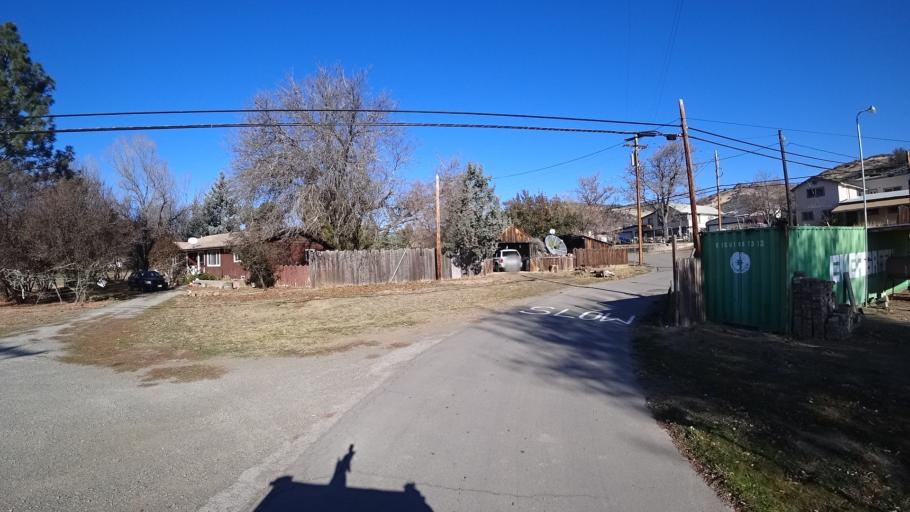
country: US
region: California
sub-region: Siskiyou County
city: Montague
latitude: 41.9112
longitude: -122.5552
